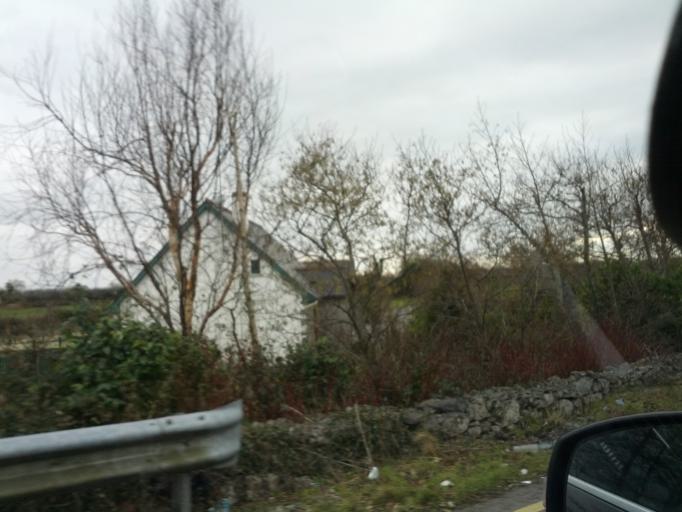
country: IE
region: Connaught
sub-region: County Galway
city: Athenry
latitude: 53.2502
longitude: -8.7487
